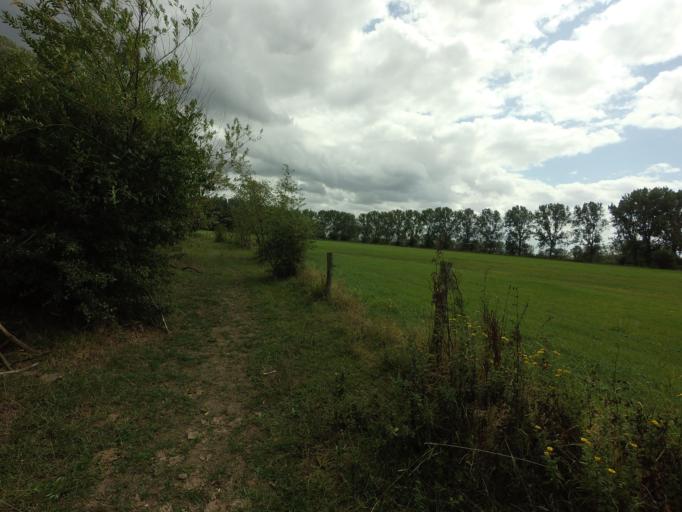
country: NL
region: Limburg
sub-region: Gemeente Maasgouw
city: Maasbracht
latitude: 51.1450
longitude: 5.8649
